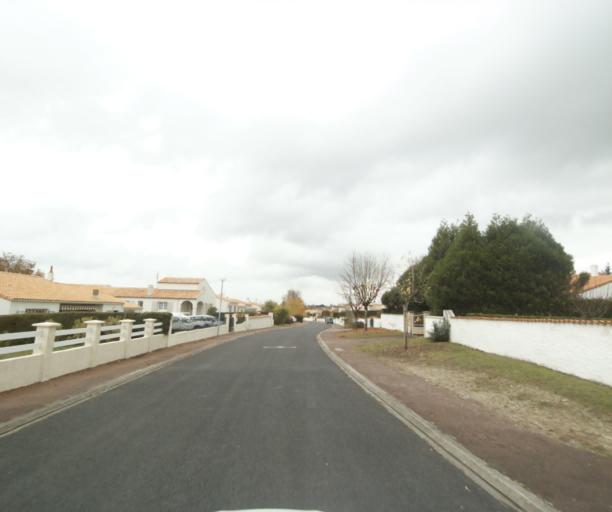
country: FR
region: Poitou-Charentes
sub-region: Departement de la Charente-Maritime
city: Saintes
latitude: 45.7395
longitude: -0.6583
